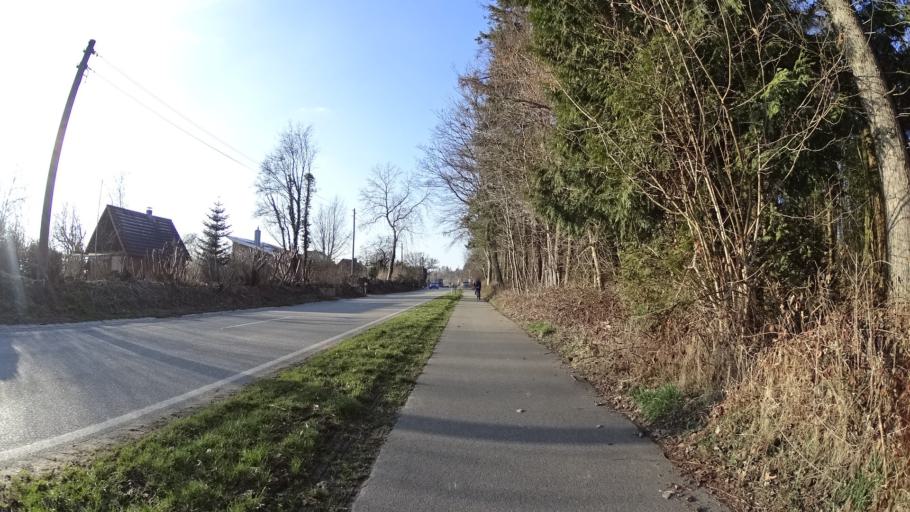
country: DE
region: Schleswig-Holstein
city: Martensrade
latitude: 54.3018
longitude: 10.3842
